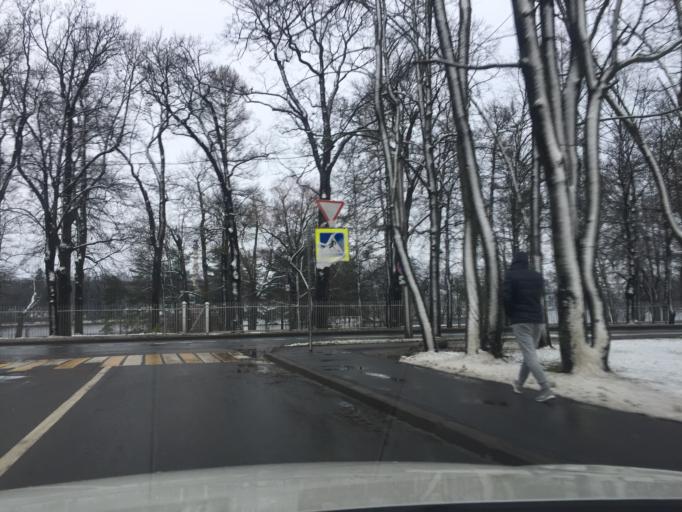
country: RU
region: St.-Petersburg
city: Pushkin
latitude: 59.7085
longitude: 30.3943
